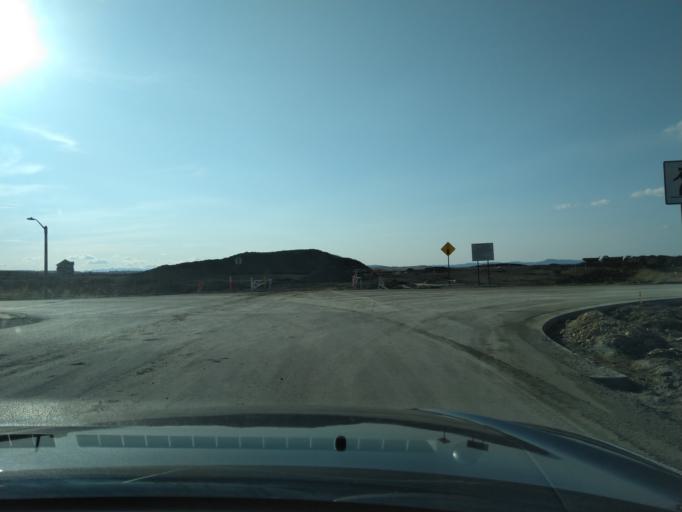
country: CA
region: Alberta
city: Cochrane
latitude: 51.1137
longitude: -114.3986
